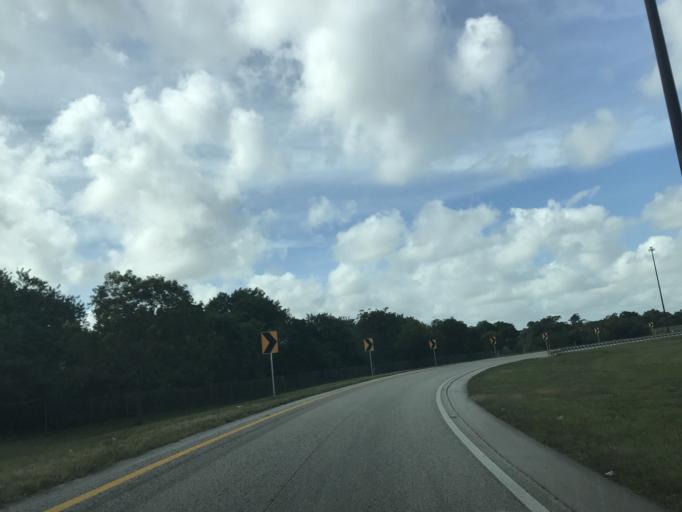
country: US
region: Florida
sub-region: Palm Beach County
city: Boca Pointe
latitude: 26.3025
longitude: -80.1667
